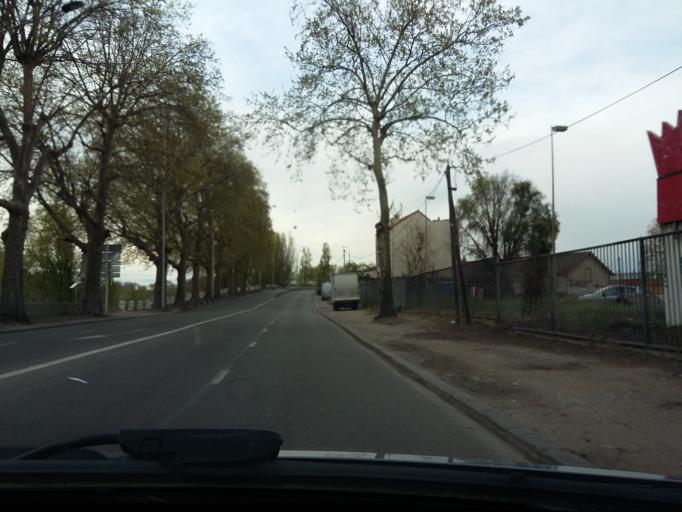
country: FR
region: Ile-de-France
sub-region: Departement de Seine-Saint-Denis
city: Villetaneuse
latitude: 48.9384
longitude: 2.3420
